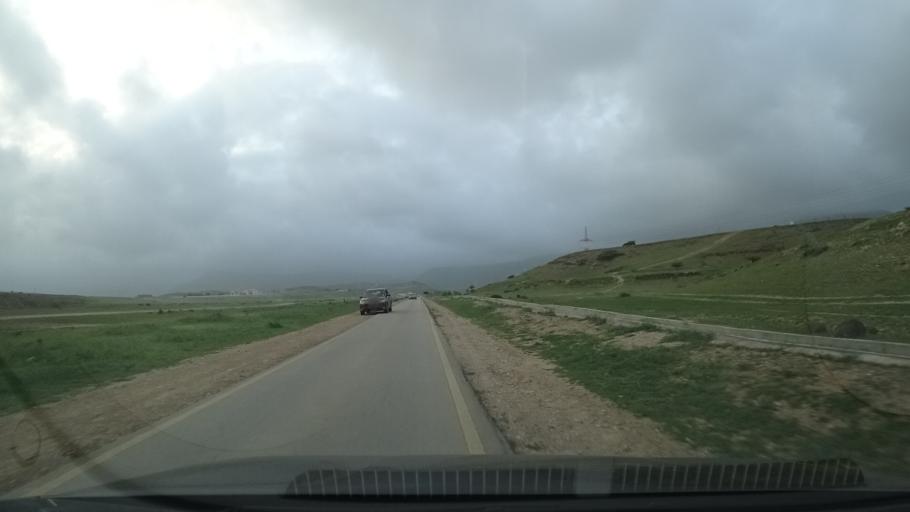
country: OM
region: Zufar
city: Salalah
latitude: 17.1101
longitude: 54.2281
